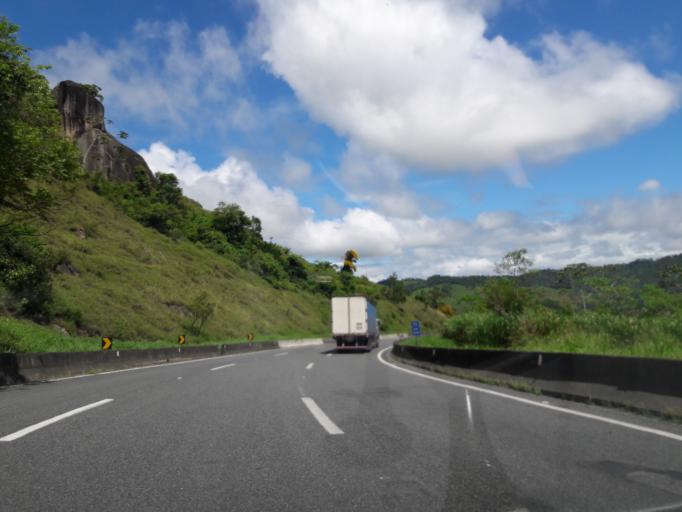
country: BR
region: Sao Paulo
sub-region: Cajati
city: Cajati
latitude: -24.9554
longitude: -48.4529
